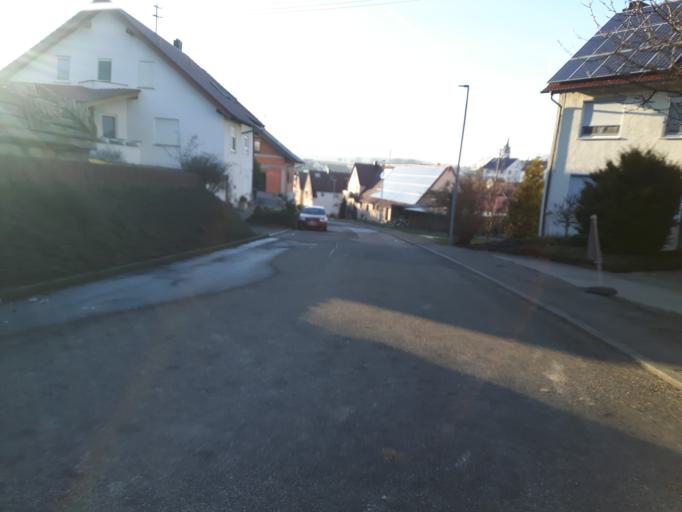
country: DE
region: Baden-Wuerttemberg
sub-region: Regierungsbezirk Stuttgart
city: Schwaigern
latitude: 49.1630
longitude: 9.0691
